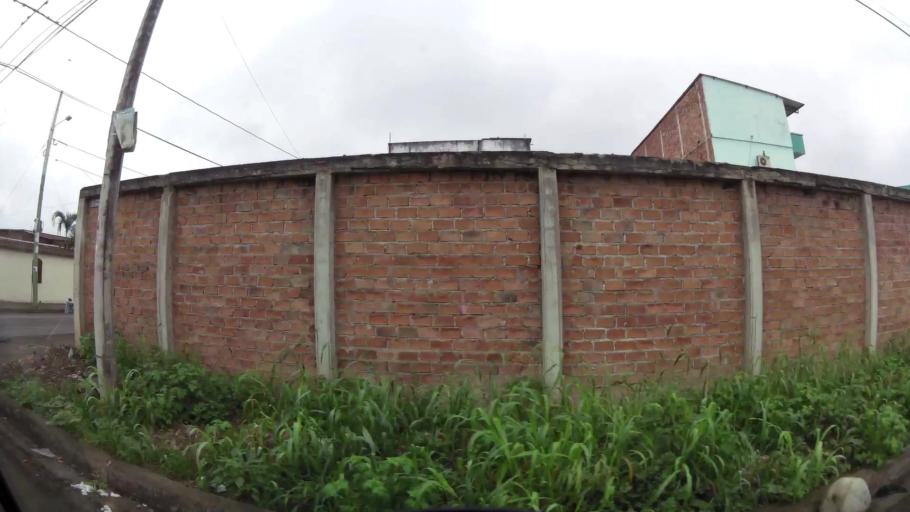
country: EC
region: El Oro
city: Pasaje
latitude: -3.3212
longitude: -79.8117
